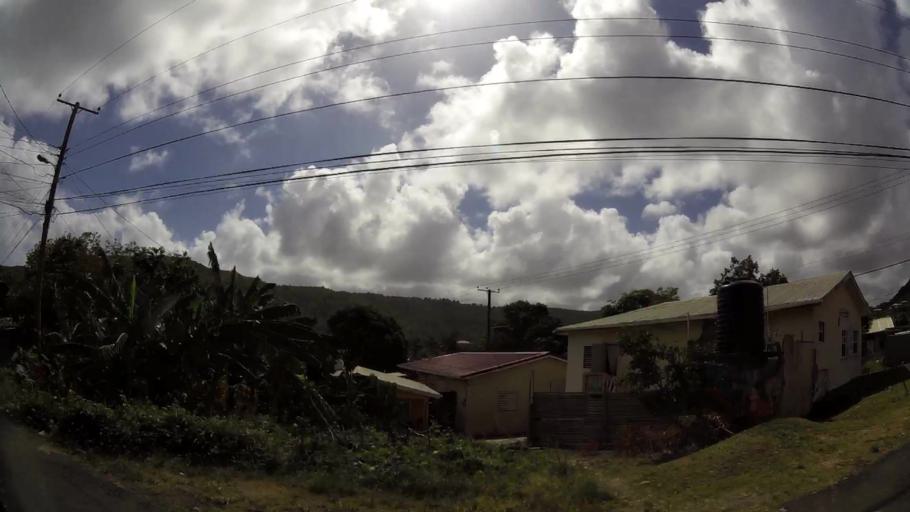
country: LC
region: Dennery Quarter
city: Dennery
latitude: 13.9124
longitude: -60.8942
